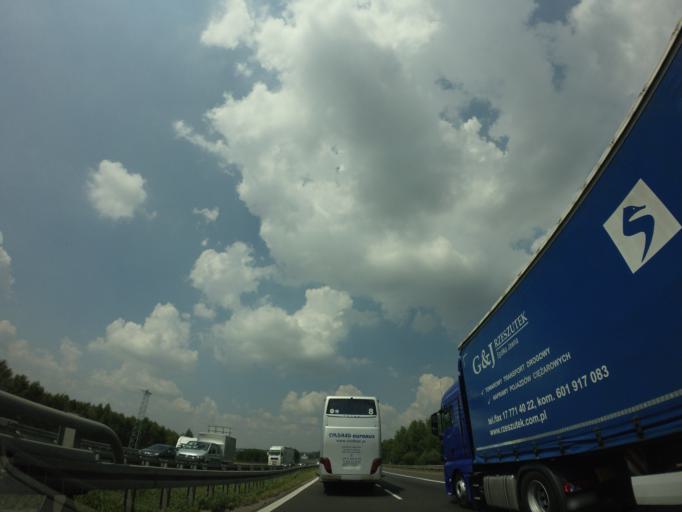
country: PL
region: Silesian Voivodeship
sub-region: Powiat gliwicki
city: Rudziniec
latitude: 50.3869
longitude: 18.4574
